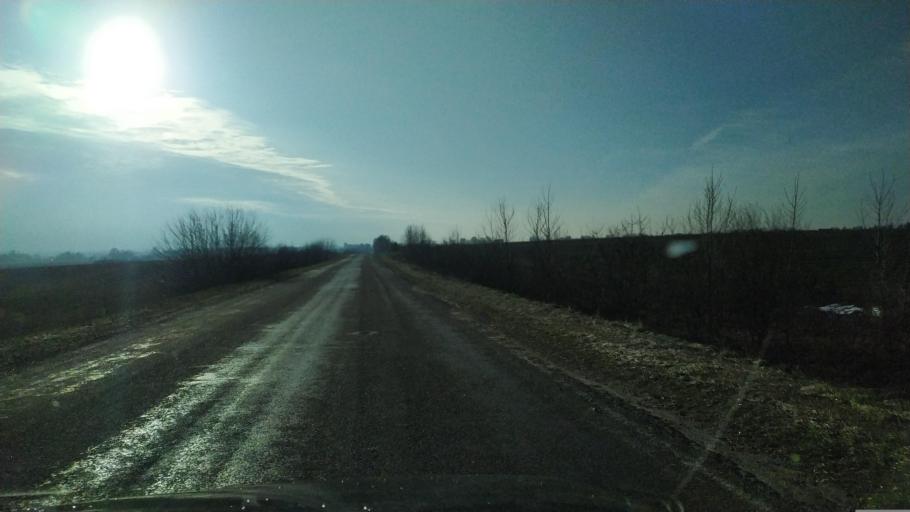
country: BY
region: Brest
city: Kamyanyets
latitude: 52.4170
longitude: 23.8041
